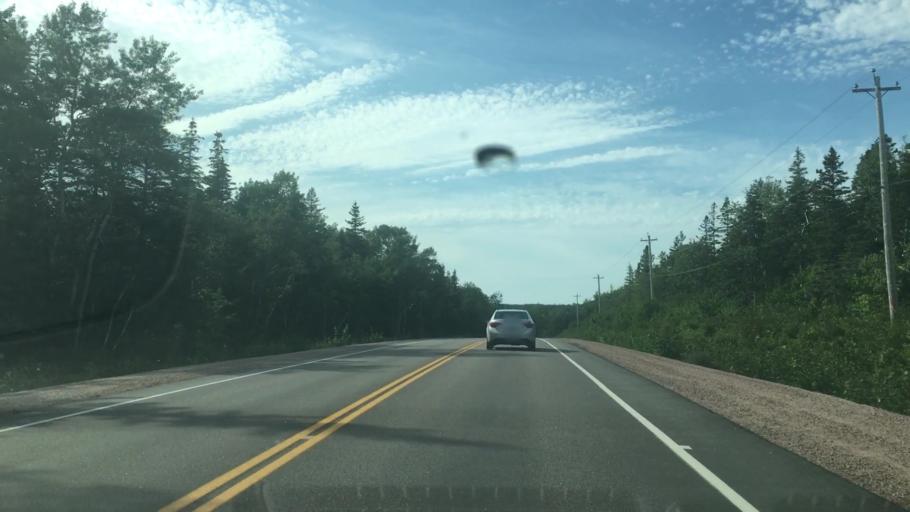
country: CA
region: Nova Scotia
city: Sydney Mines
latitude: 46.8197
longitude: -60.3518
